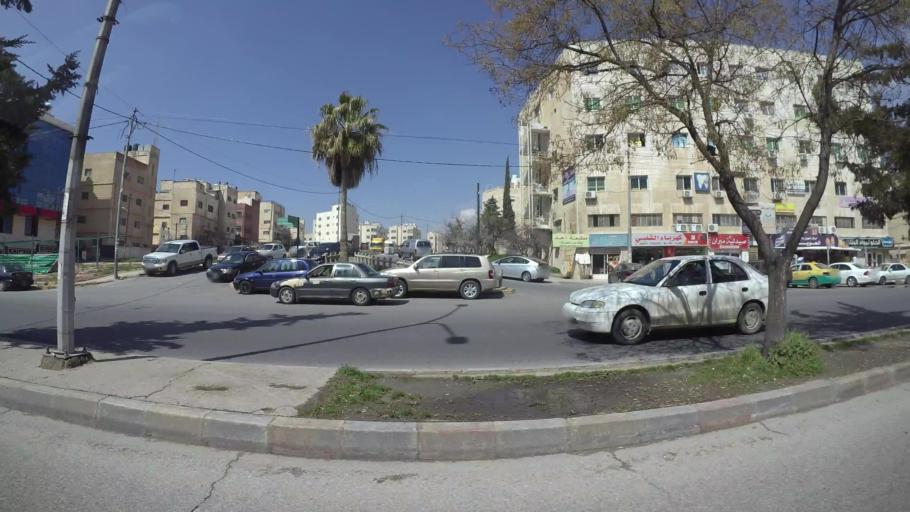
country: JO
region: Amman
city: Al Bunayyat ash Shamaliyah
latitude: 31.9265
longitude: 35.9051
